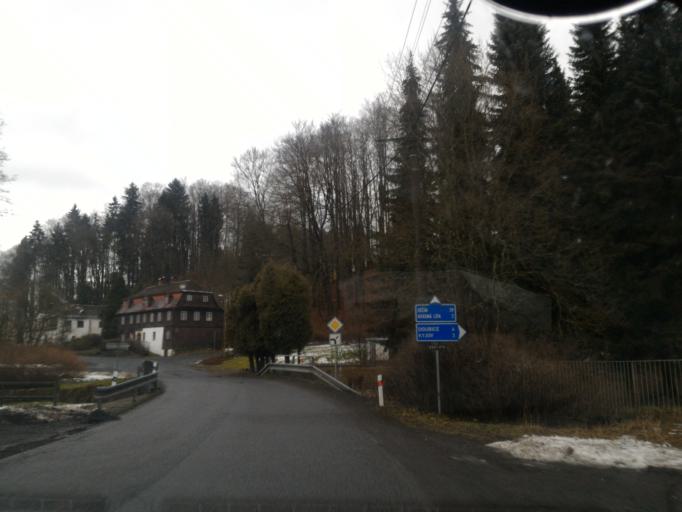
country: CZ
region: Ustecky
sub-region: Okres Decin
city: Krasna Lipa
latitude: 50.9211
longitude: 14.4894
